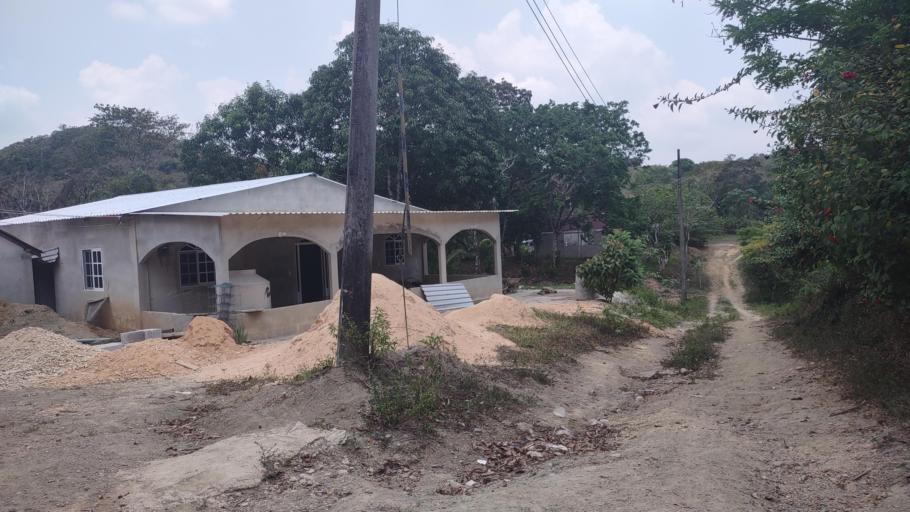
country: MX
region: Tabasco
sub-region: Huimanguillo
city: Francisco Rueda
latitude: 17.6487
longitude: -93.9064
